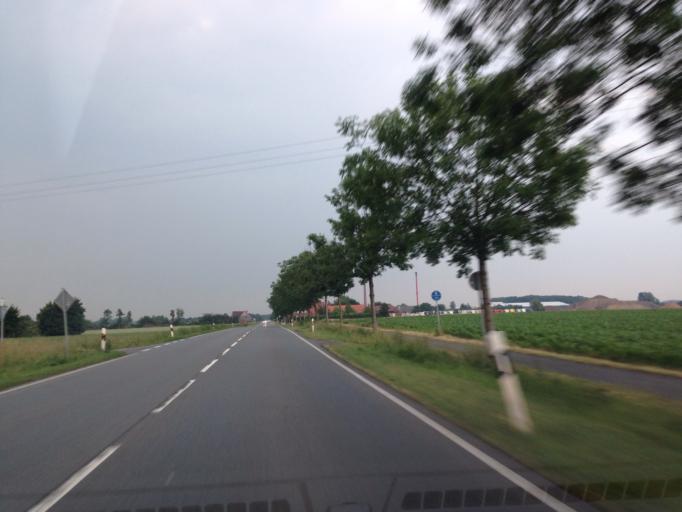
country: DE
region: North Rhine-Westphalia
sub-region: Regierungsbezirk Munster
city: Nottuln
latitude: 51.9189
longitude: 7.3785
